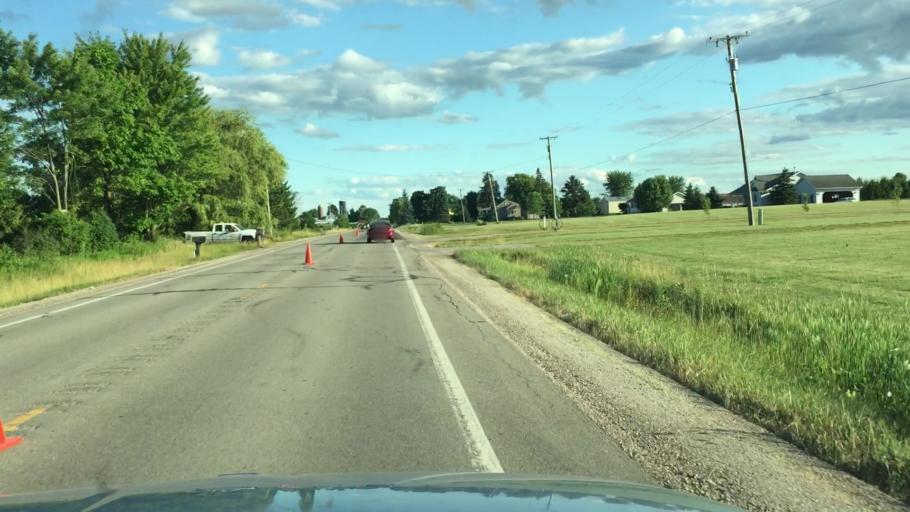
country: US
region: Michigan
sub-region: Saint Clair County
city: Yale
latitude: 43.0981
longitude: -82.7667
